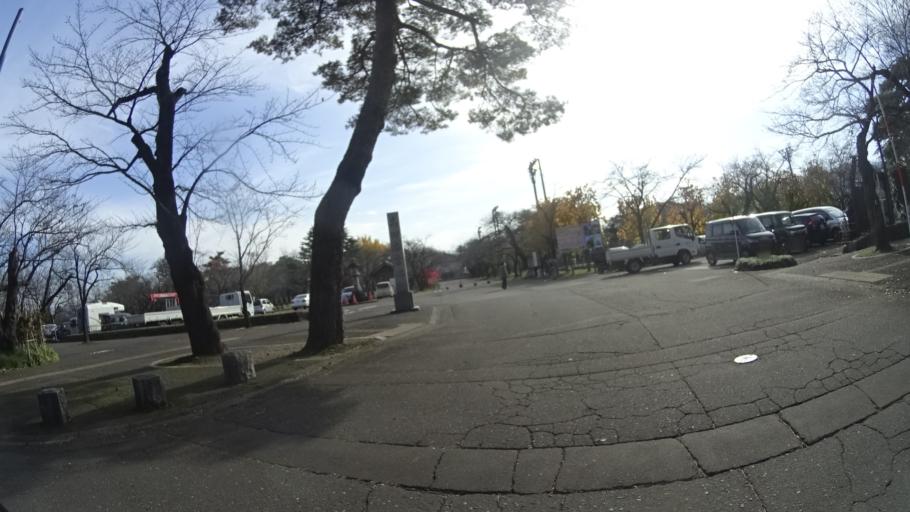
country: JP
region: Niigata
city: Joetsu
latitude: 37.1091
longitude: 138.2549
